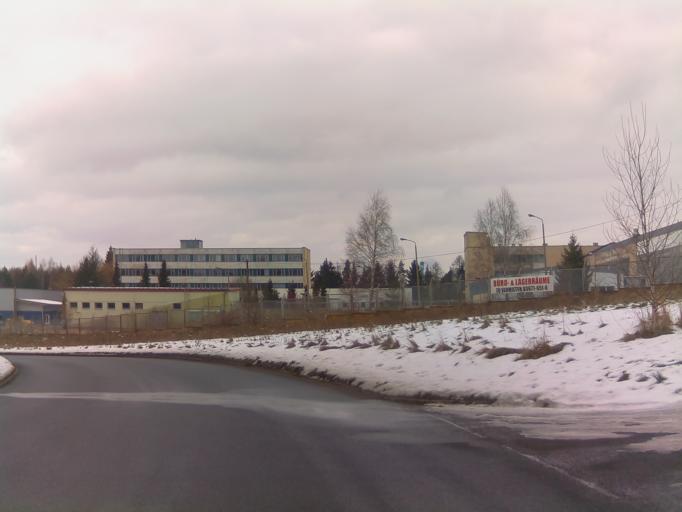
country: DE
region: Thuringia
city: Neuhaus
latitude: 50.6914
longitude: 10.9547
